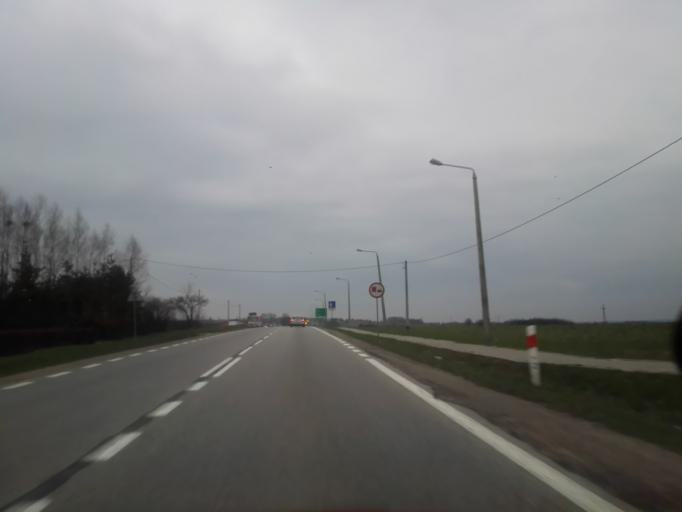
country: PL
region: Podlasie
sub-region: Powiat lomzynski
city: Piatnica
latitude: 53.2468
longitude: 22.1187
